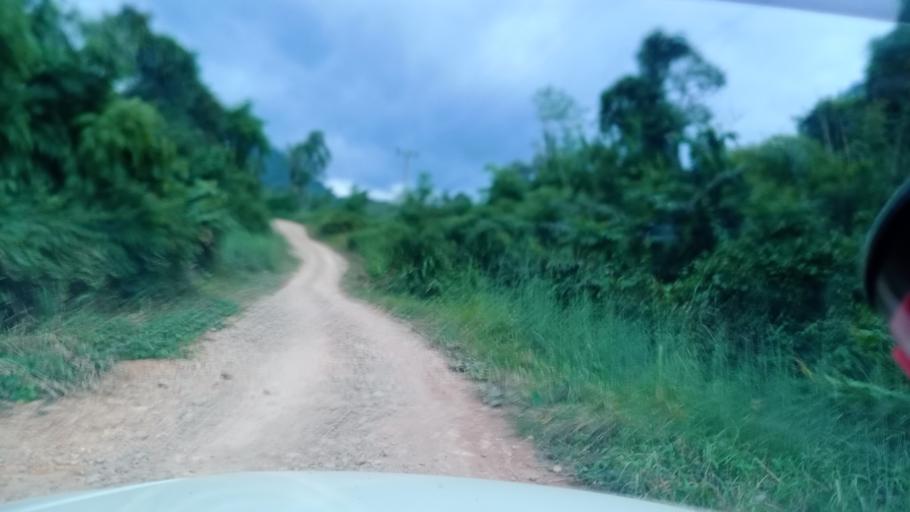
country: TH
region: Changwat Bueng Kan
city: Pak Khat
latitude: 18.7247
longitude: 103.2581
